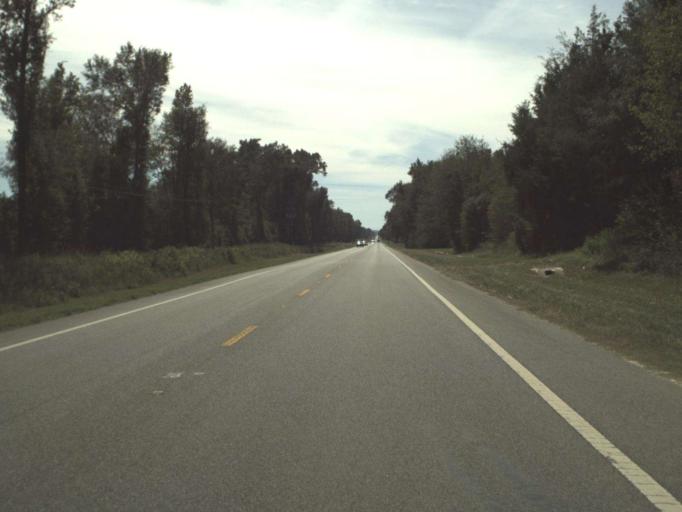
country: US
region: Florida
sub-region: Washington County
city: Chipley
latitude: 30.7098
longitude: -85.5588
